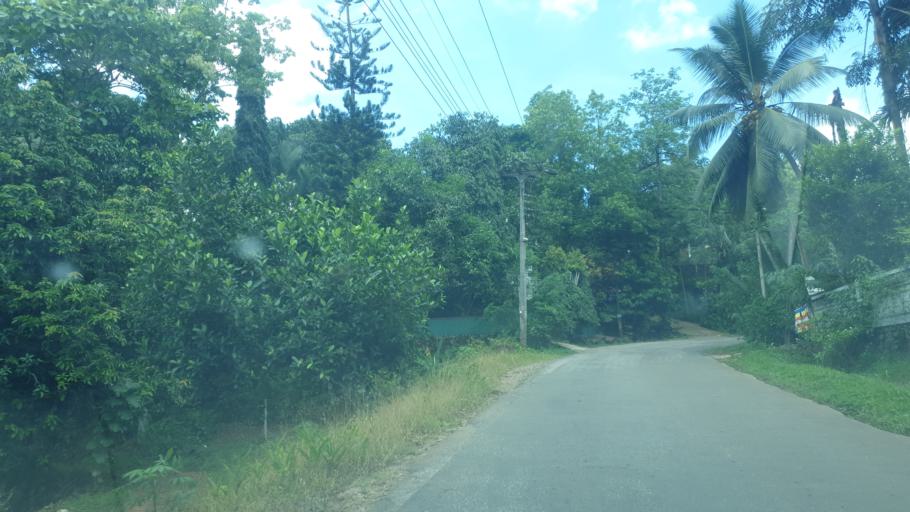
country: LK
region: Sabaragamuwa
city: Ratnapura
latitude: 6.4898
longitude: 80.4004
